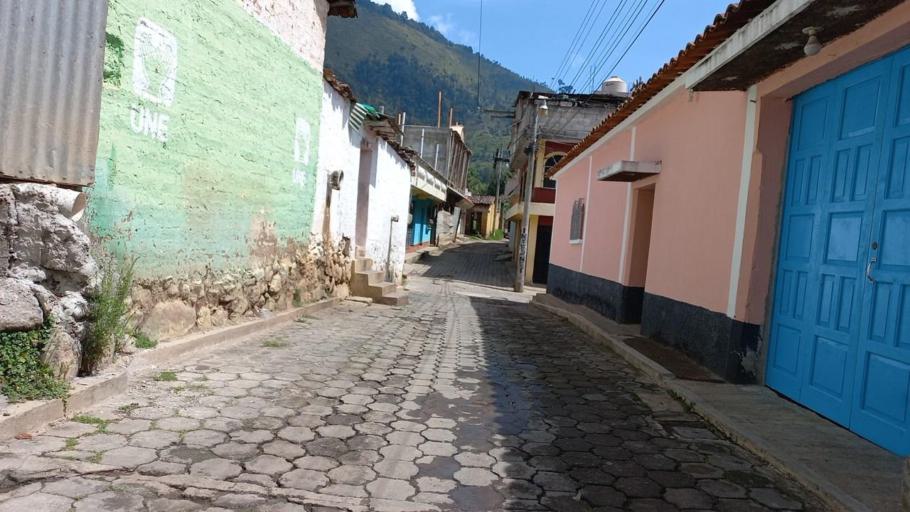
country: GT
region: Totonicapan
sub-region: Municipio de San Andres Xecul
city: San Andres Xecul
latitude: 14.9064
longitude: -91.4824
